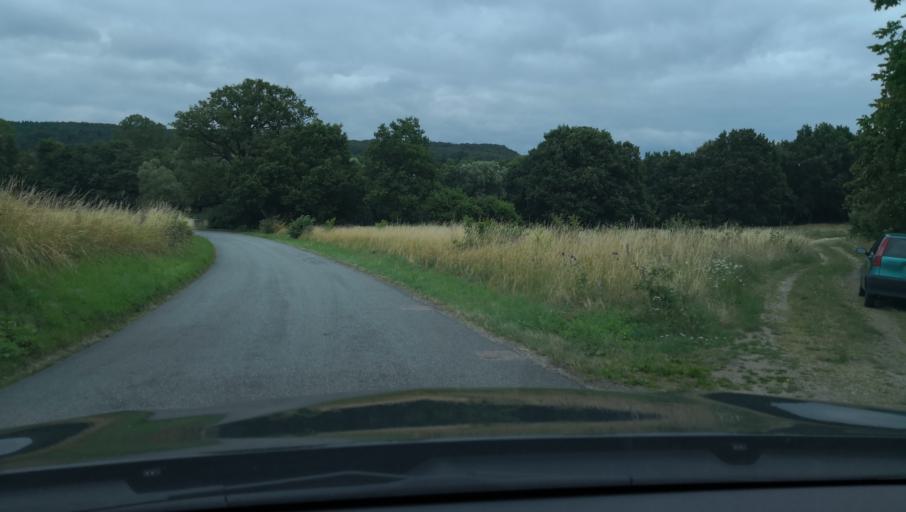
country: SE
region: Skane
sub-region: Simrishamns Kommun
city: Kivik
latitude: 55.7186
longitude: 14.1572
